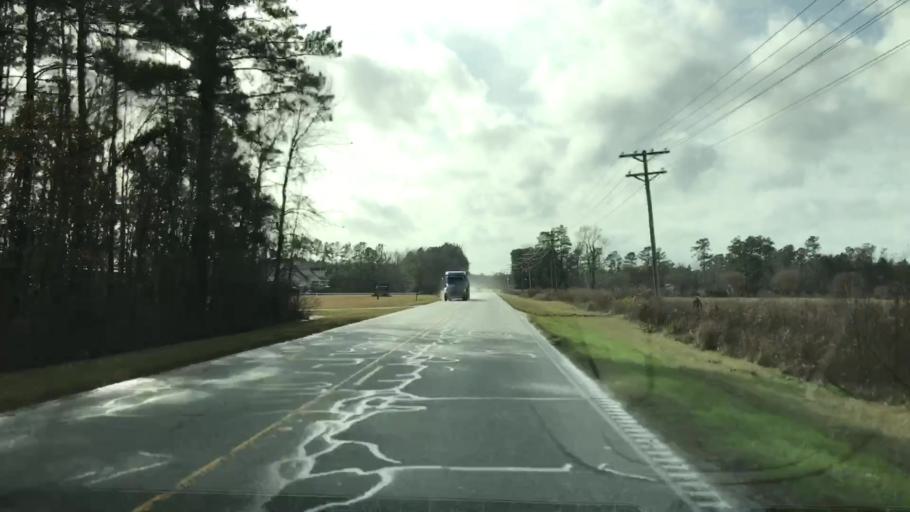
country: US
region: South Carolina
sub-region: Williamsburg County
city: Andrews
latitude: 33.4986
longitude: -79.5345
